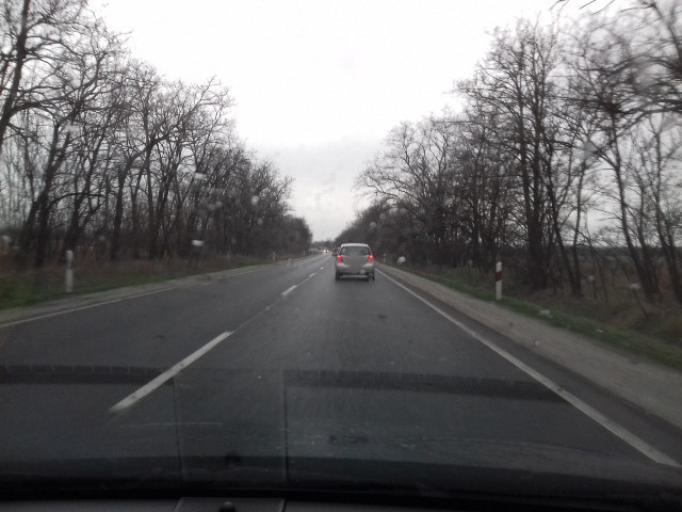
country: HU
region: Szabolcs-Szatmar-Bereg
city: Ujfeherto
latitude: 47.8354
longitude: 21.7032
